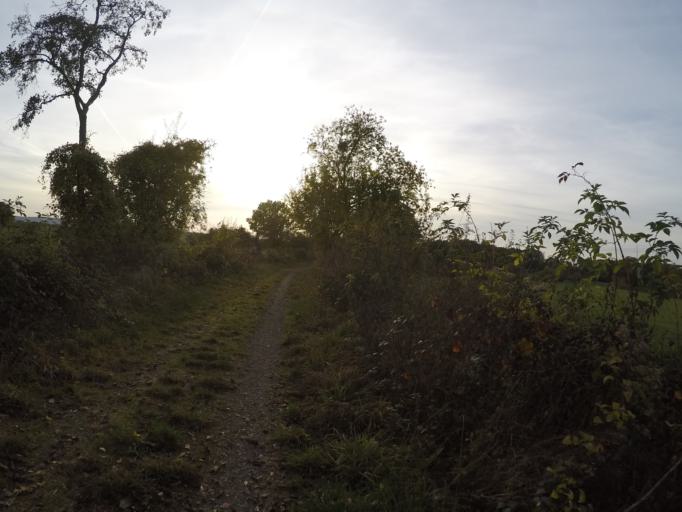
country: BE
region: Wallonia
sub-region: Province du Luxembourg
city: Hotton
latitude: 50.2862
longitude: 5.4941
